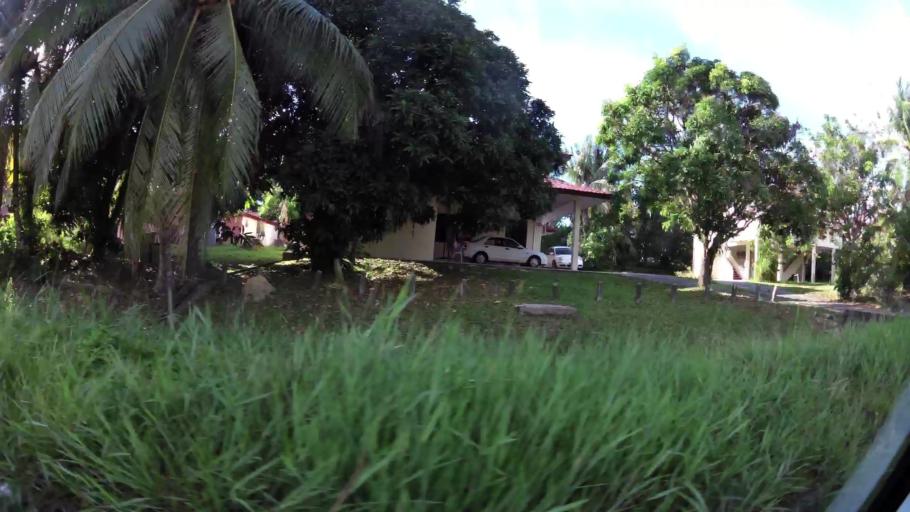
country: BN
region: Brunei and Muara
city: Bandar Seri Begawan
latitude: 4.9861
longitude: 114.9665
